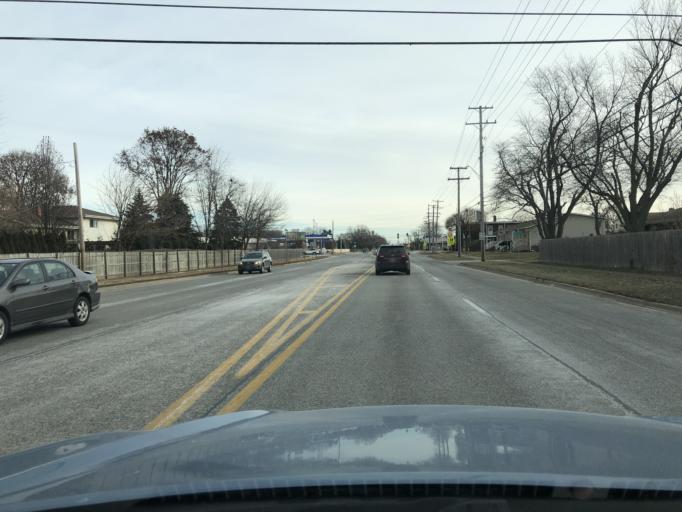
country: US
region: Illinois
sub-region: Cook County
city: Mount Prospect
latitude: 42.0662
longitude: -87.9104
